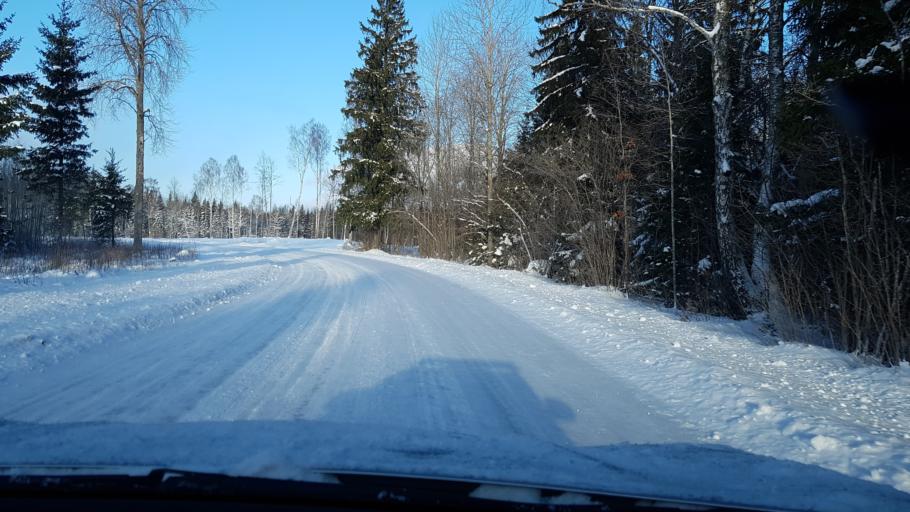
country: EE
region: Harju
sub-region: Nissi vald
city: Turba
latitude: 59.1171
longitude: 24.2218
